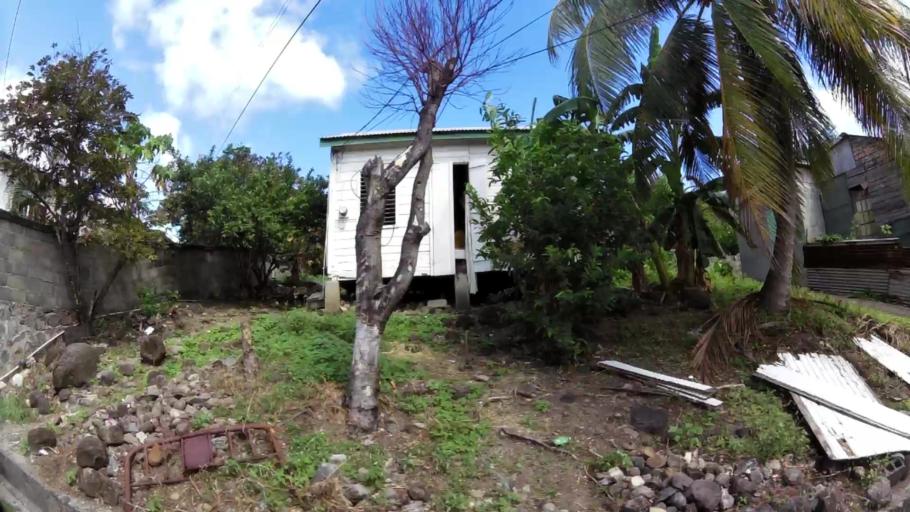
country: LC
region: Micoud Quarter
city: Micoud
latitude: 13.8214
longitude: -60.8967
